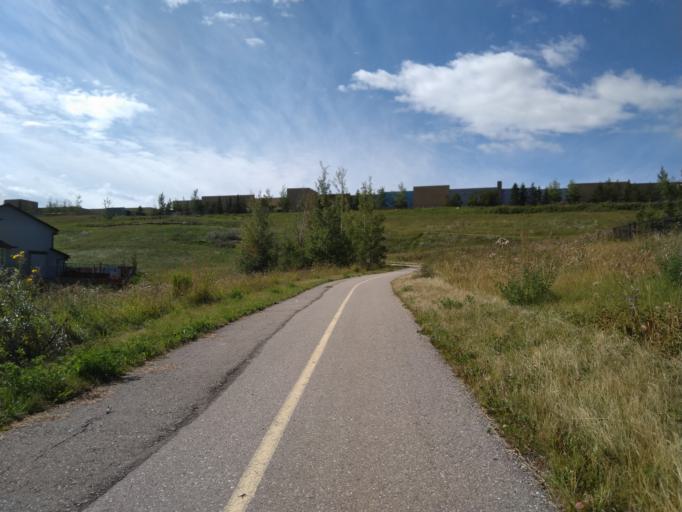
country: CA
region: Alberta
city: Calgary
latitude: 51.1596
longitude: -114.1565
